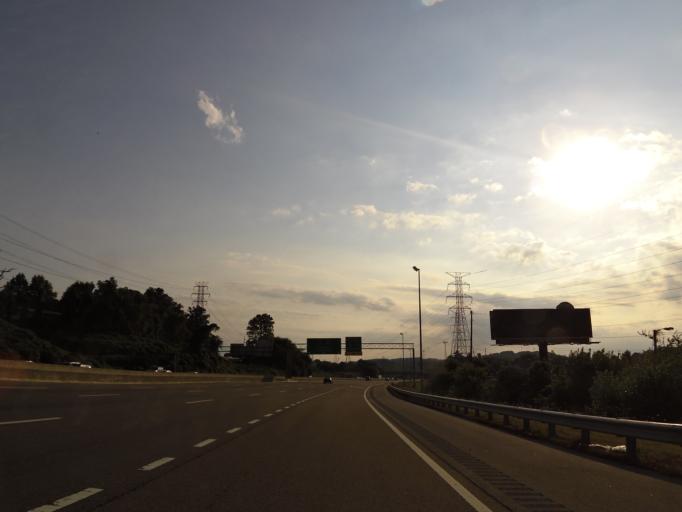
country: US
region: Tennessee
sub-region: Knox County
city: Knoxville
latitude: 35.9596
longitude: -83.9593
